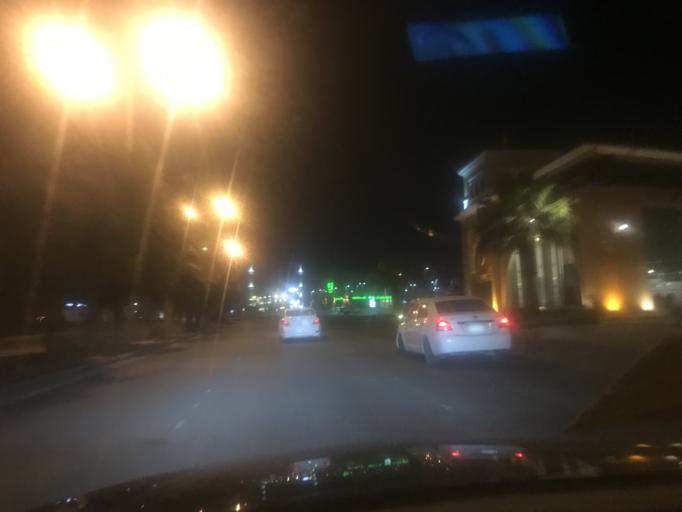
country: SA
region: Ar Riyad
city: Riyadh
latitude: 24.6933
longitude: 46.6074
